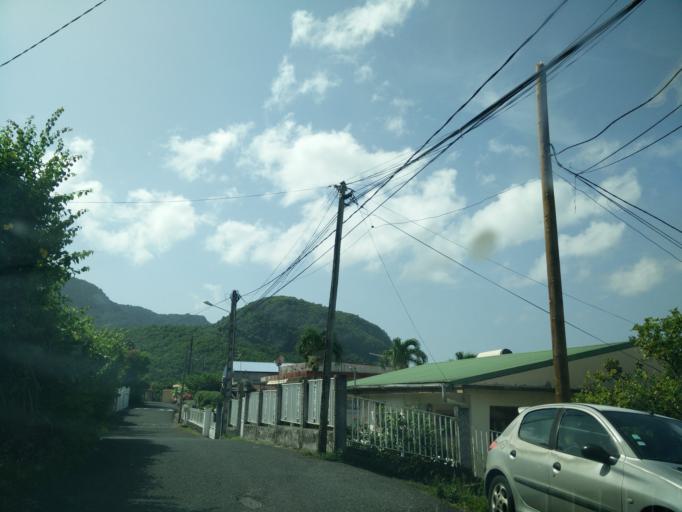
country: GP
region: Guadeloupe
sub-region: Guadeloupe
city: Gourbeyre
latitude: 15.9938
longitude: -61.7074
